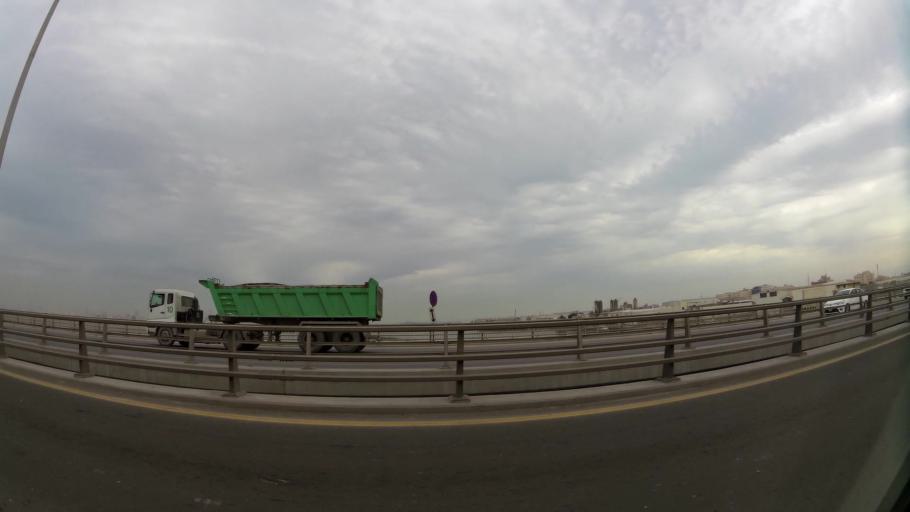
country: BH
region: Northern
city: Sitrah
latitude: 26.1750
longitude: 50.5968
